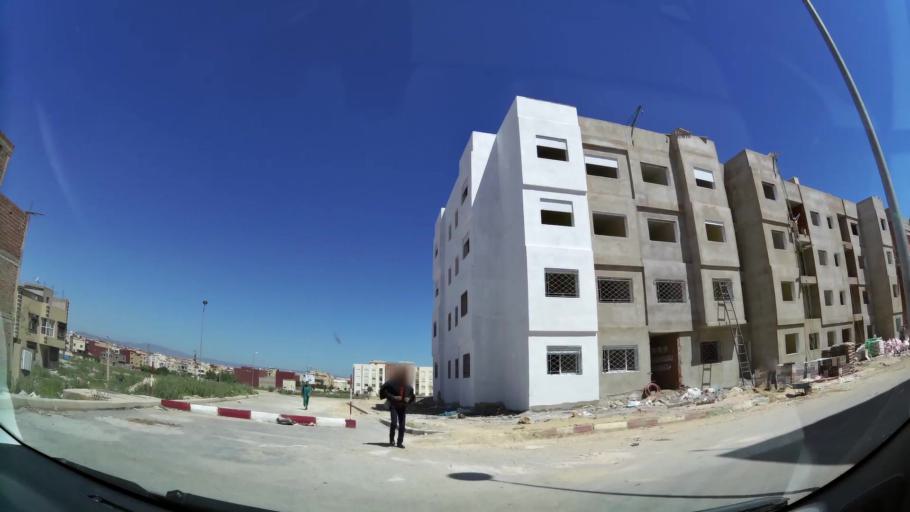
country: MA
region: Oriental
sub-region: Oujda-Angad
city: Oujda
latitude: 34.6538
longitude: -1.8819
